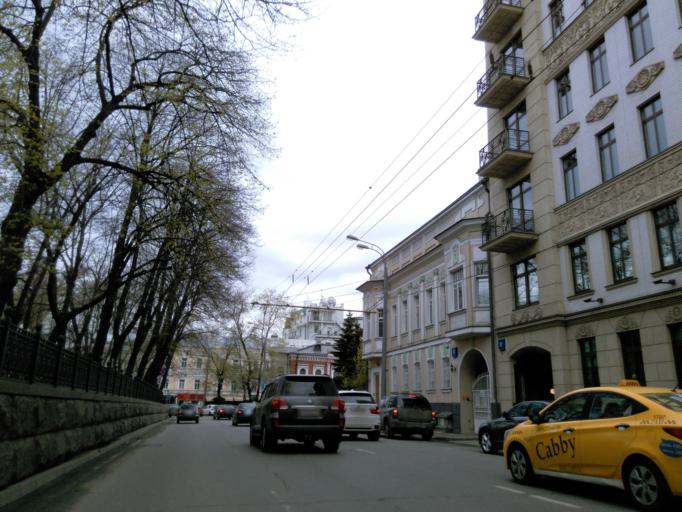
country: RU
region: Moscow
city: Moscow
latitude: 55.7460
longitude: 37.5997
